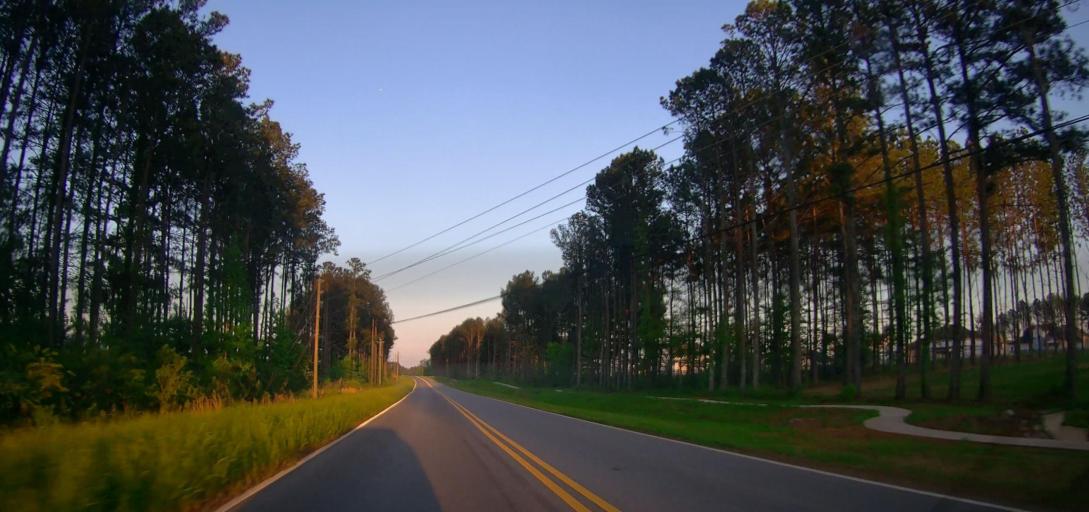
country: US
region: Georgia
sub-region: Henry County
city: McDonough
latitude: 33.4041
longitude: -84.1279
